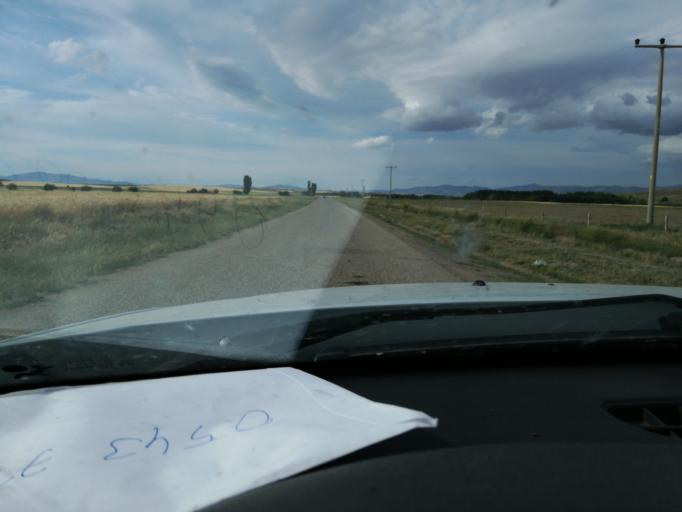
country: TR
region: Kirsehir
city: Kirsehir
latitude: 39.0038
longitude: 34.1196
